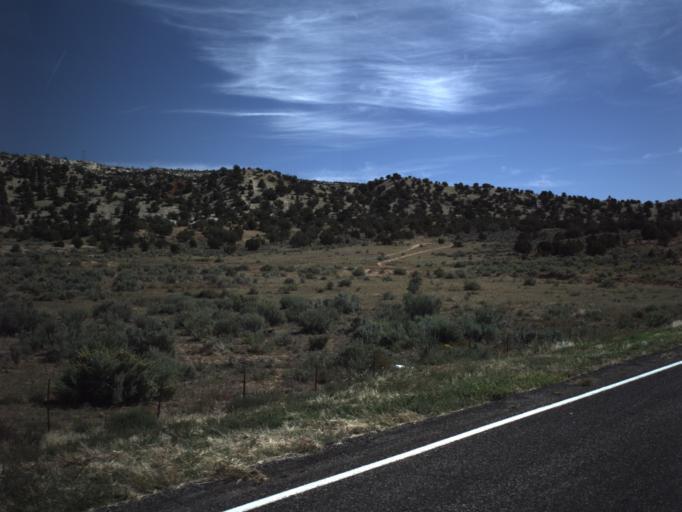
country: US
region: Utah
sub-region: Wayne County
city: Loa
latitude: 37.7608
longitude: -111.5778
